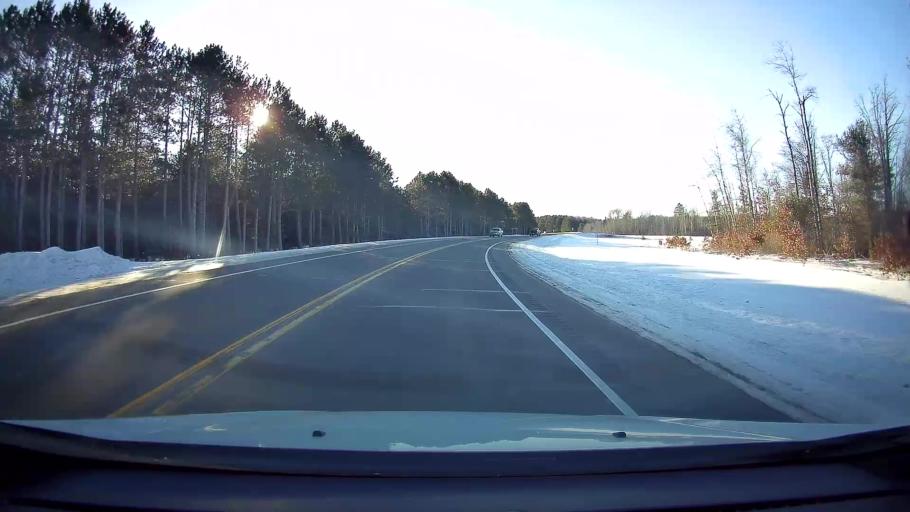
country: US
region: Wisconsin
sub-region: Sawyer County
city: Hayward
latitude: 45.9940
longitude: -91.5933
